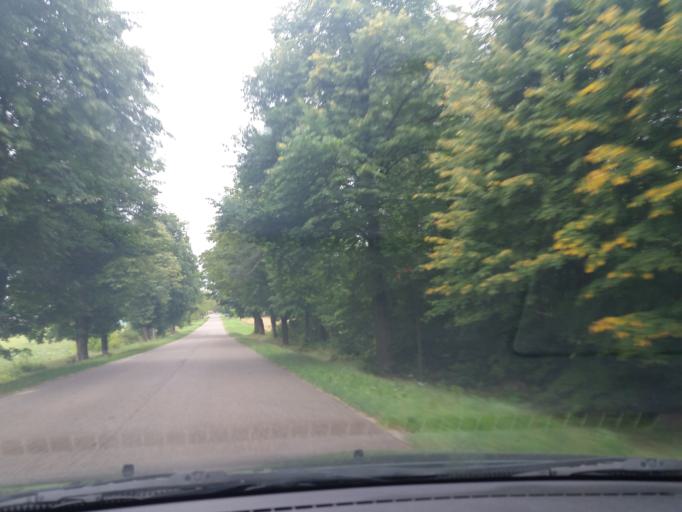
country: PL
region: Masovian Voivodeship
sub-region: Powiat mlawski
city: Wieczfnia Koscielna
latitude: 53.2035
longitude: 20.4938
